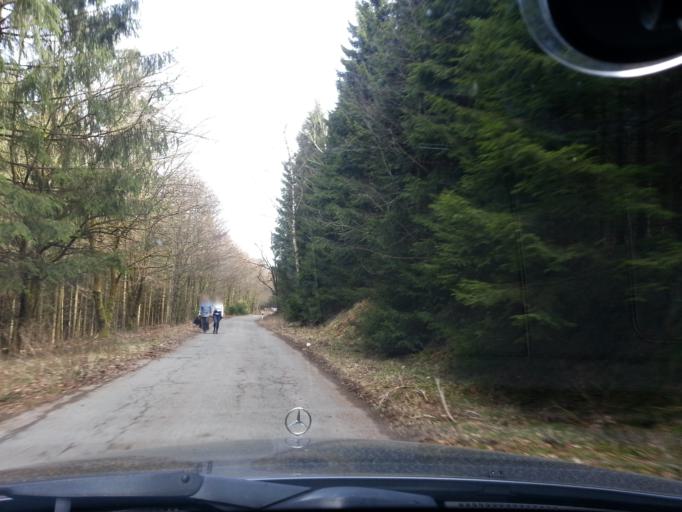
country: DE
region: North Rhine-Westphalia
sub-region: Regierungsbezirk Arnsberg
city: Bad Fredeburg
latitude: 51.2116
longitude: 8.3430
